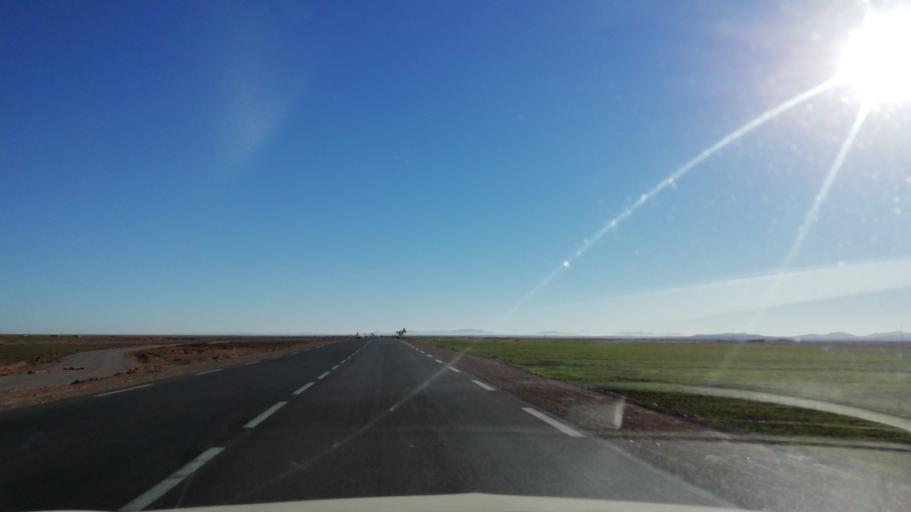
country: DZ
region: El Bayadh
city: El Bayadh
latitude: 33.8595
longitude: 0.5626
